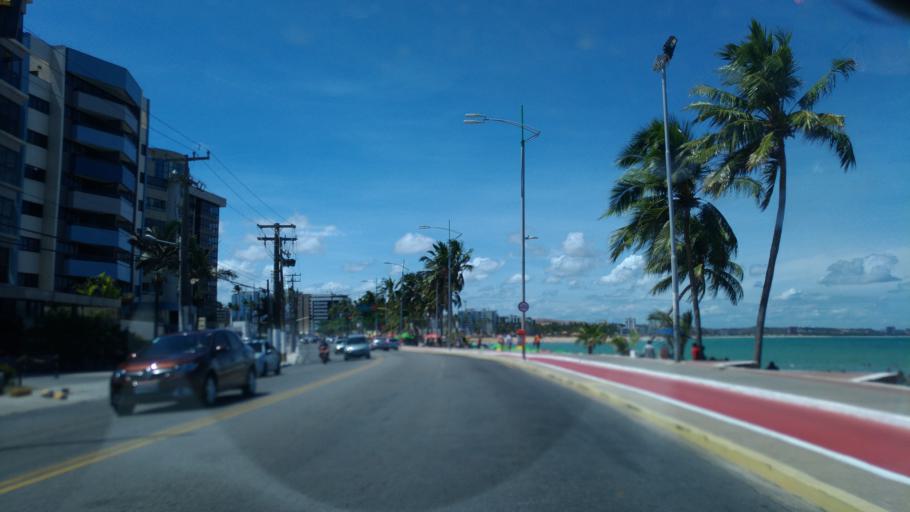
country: BR
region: Alagoas
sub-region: Maceio
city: Maceio
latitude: -9.6526
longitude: -35.6989
